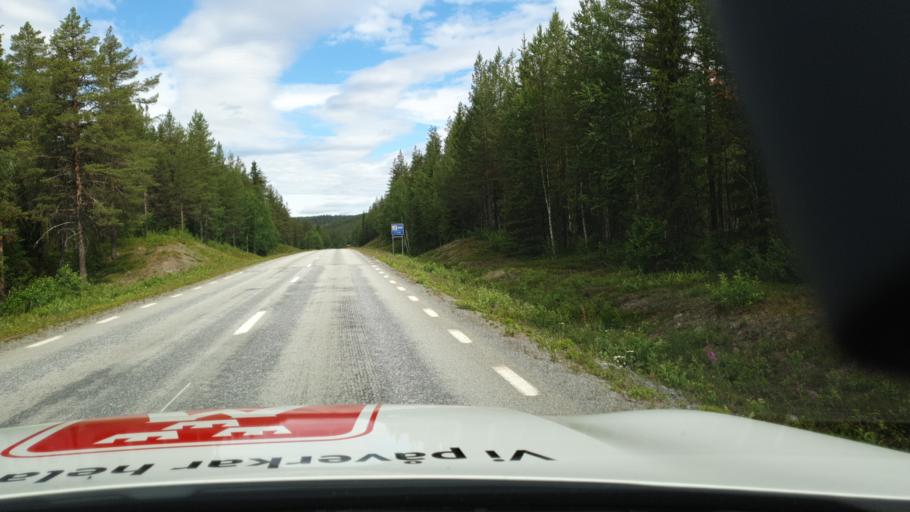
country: SE
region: Vaesterbotten
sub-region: Storumans Kommun
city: Fristad
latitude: 65.3716
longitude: 16.5176
